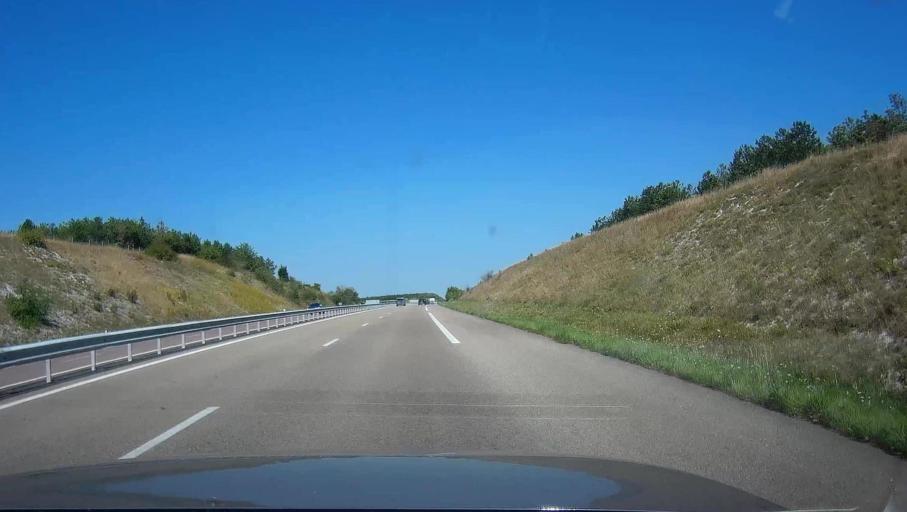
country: FR
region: Champagne-Ardenne
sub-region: Departement de l'Aube
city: Creney-pres-Troyes
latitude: 48.3681
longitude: 4.1593
